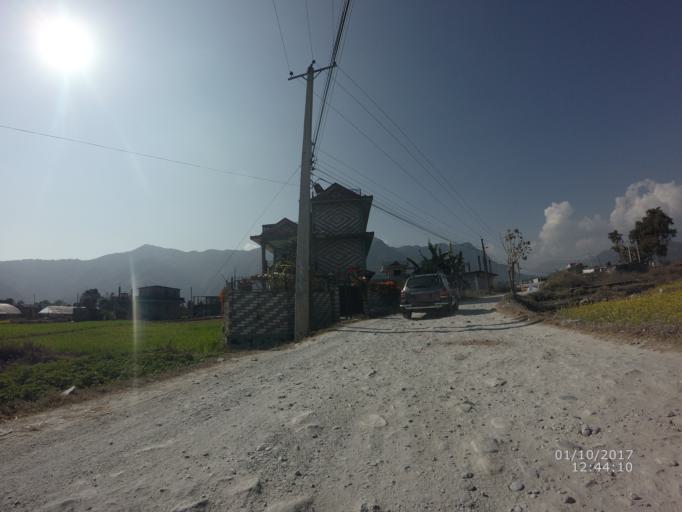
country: NP
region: Western Region
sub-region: Gandaki Zone
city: Pokhara
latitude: 28.2685
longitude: 83.9633
